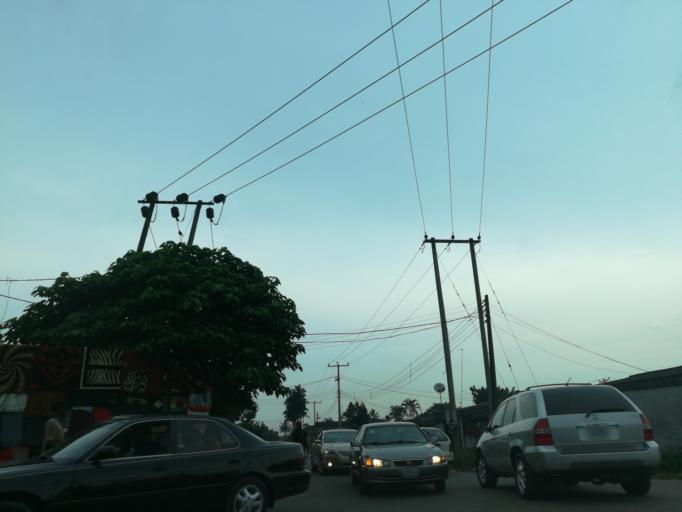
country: NG
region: Rivers
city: Port Harcourt
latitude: 4.8190
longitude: 7.0295
